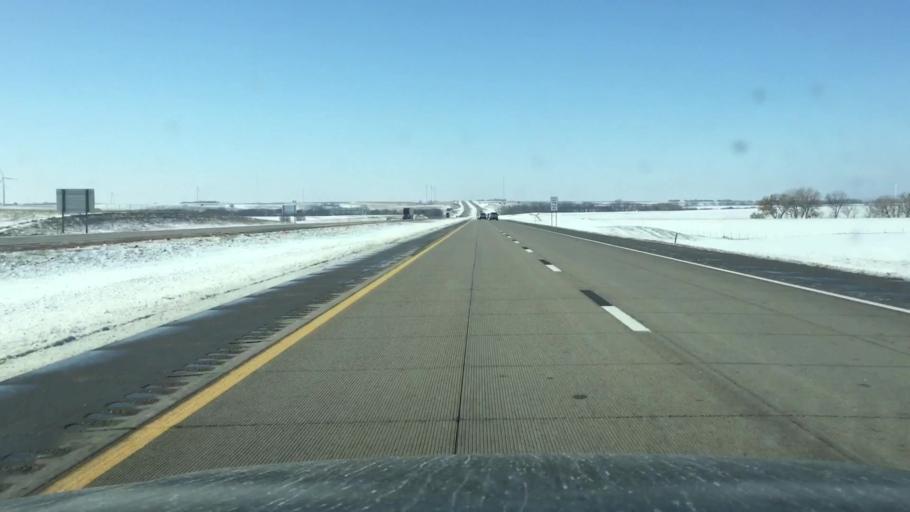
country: US
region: Kansas
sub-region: Ellsworth County
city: Ellsworth
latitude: 38.8494
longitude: -98.2902
